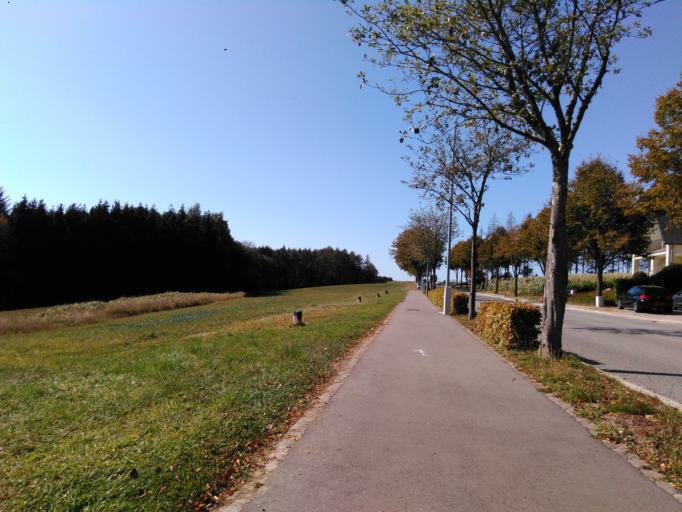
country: LU
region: Diekirch
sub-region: Canton de Redange
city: Rambrouch
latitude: 49.8396
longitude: 5.8331
